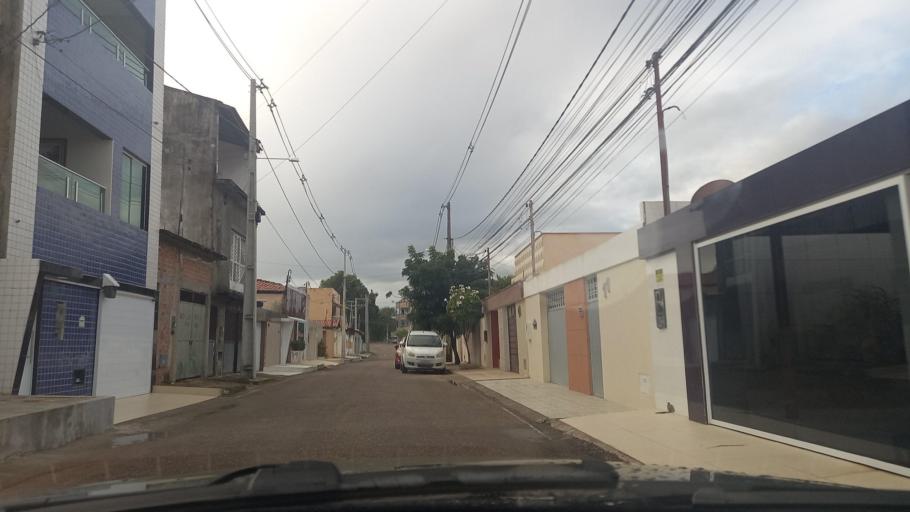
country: BR
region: Bahia
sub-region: Paulo Afonso
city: Paulo Afonso
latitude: -9.3956
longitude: -38.2148
